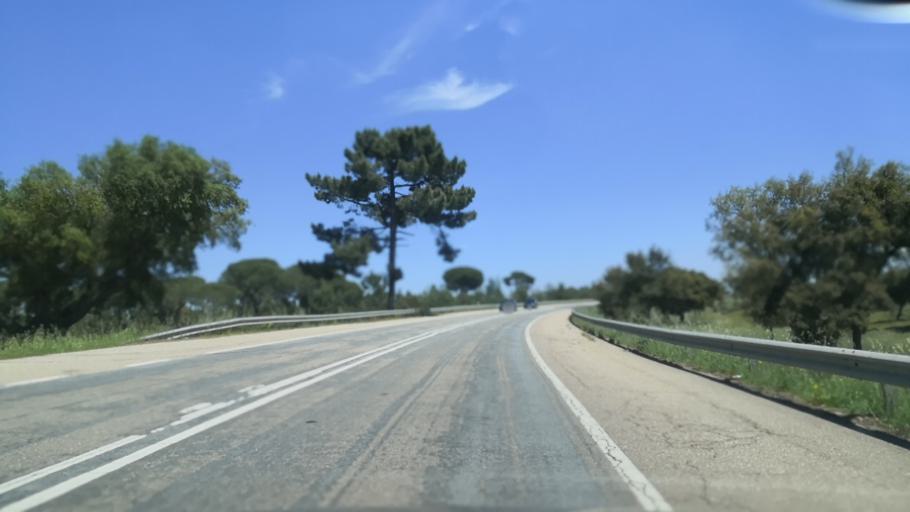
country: PT
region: Evora
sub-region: Vendas Novas
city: Vendas Novas
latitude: 38.6856
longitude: -8.5292
